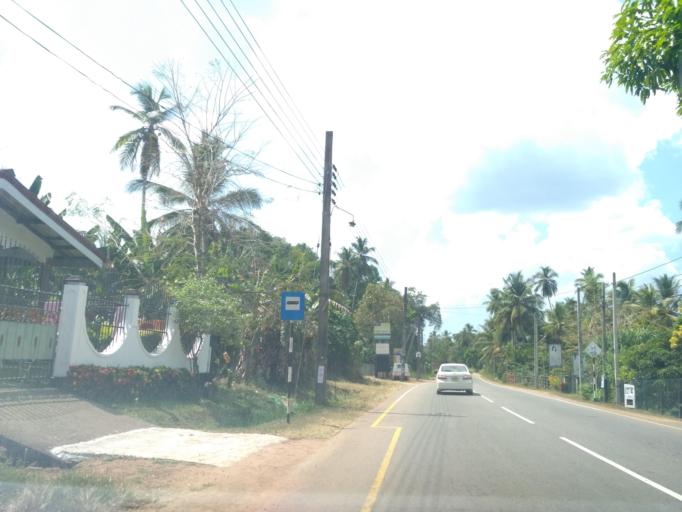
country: LK
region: North Western
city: Kuliyapitiya
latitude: 7.3270
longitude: 80.0534
